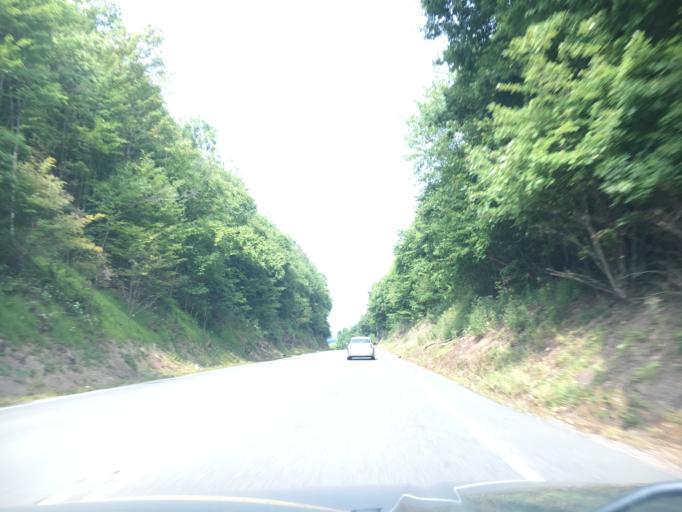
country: US
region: Pennsylvania
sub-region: Carbon County
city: Summit Hill
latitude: 40.7093
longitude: -75.8280
